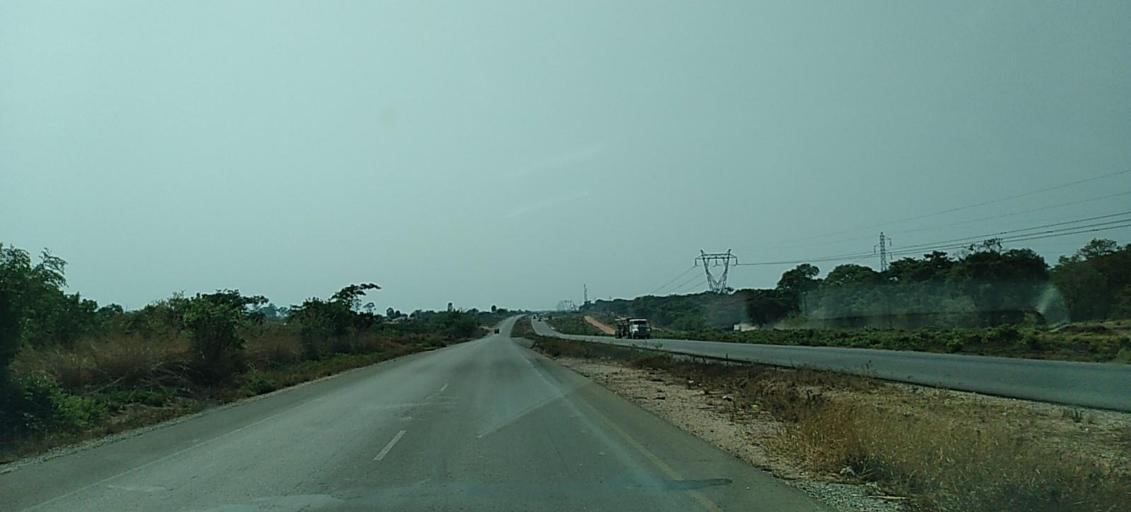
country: ZM
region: Copperbelt
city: Chingola
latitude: -12.5863
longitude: 27.9389
